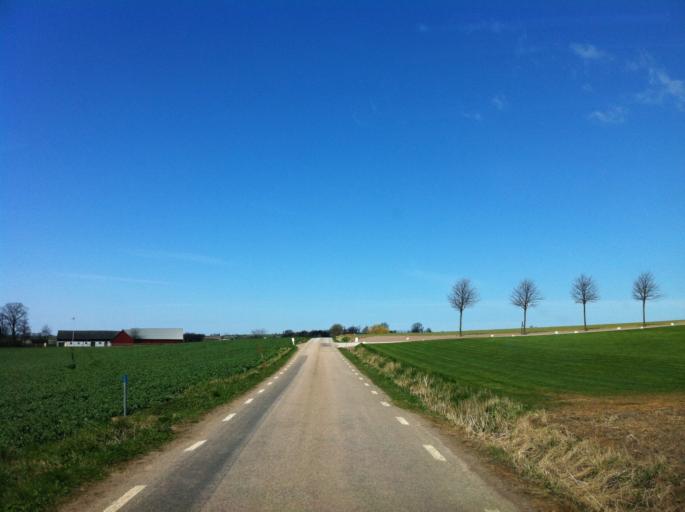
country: SE
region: Skane
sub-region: Landskrona
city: Asmundtorp
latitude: 55.9109
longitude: 12.8874
